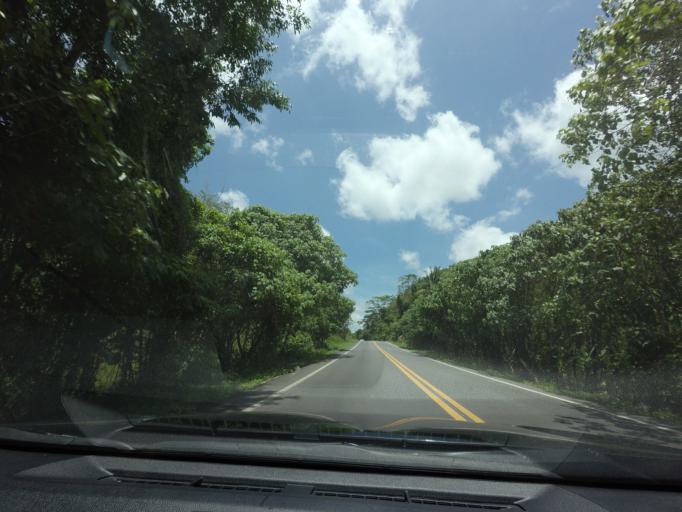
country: TH
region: Chumphon
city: Ban Nam Yuen
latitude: 9.9083
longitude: 98.9094
